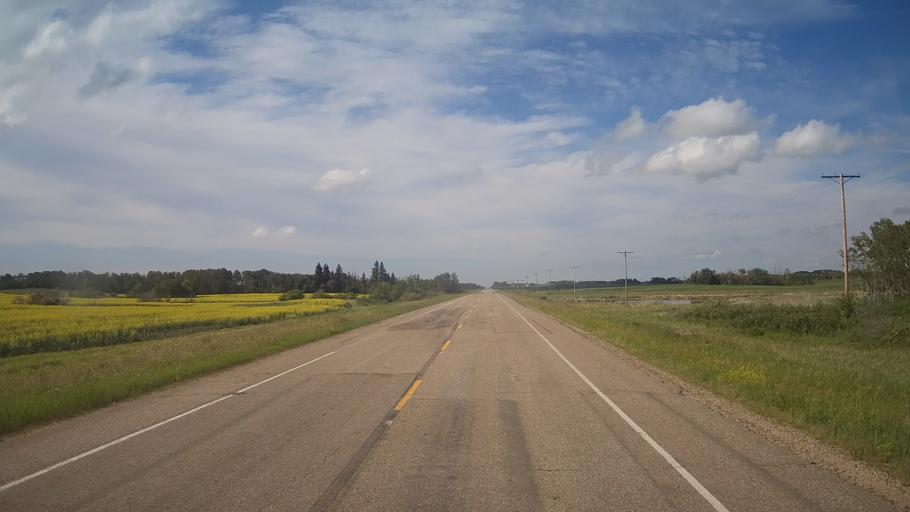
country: CA
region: Saskatchewan
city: Foam Lake
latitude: 51.5678
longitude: -103.8457
